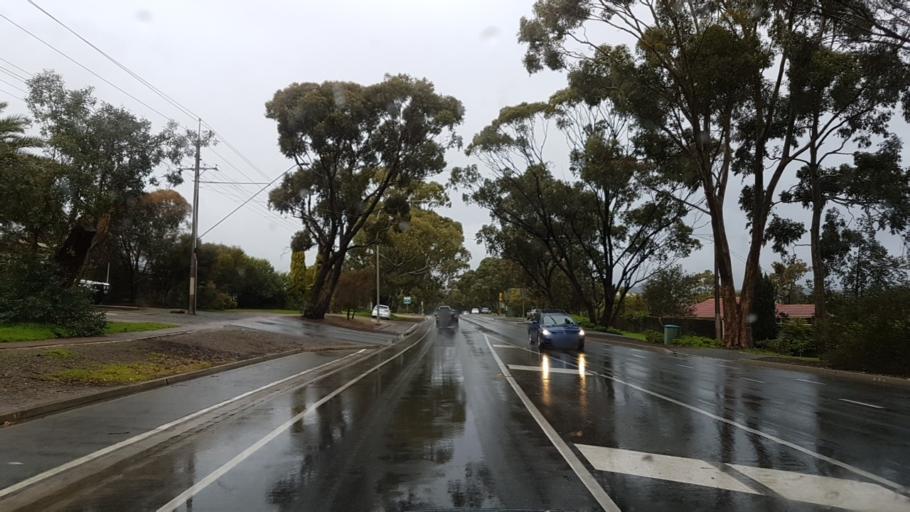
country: AU
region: South Australia
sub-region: Onkaparinga
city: Craigburn Farm
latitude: -35.0523
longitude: 138.5925
